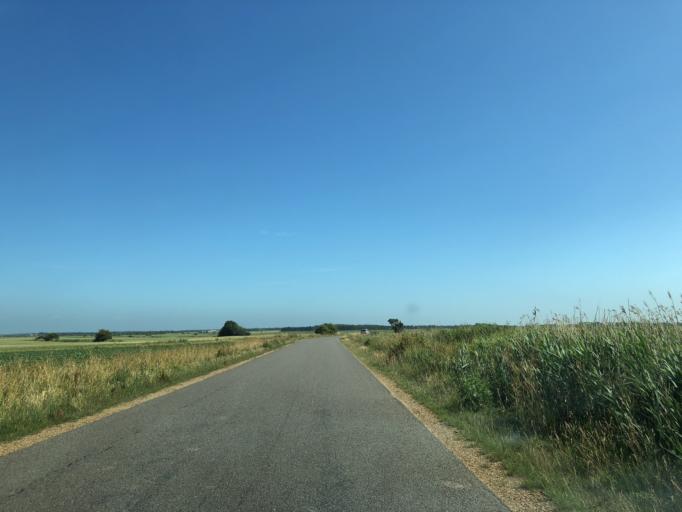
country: DK
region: Central Jutland
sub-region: Holstebro Kommune
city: Ulfborg
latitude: 56.2932
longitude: 8.2136
